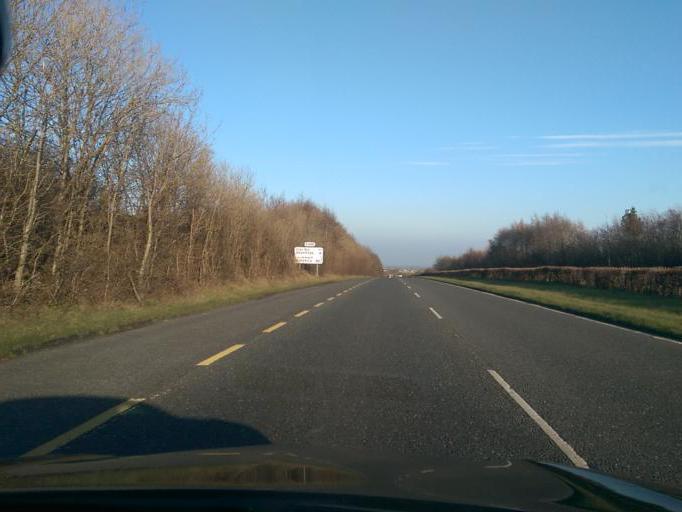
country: IE
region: Connaught
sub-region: County Galway
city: Oranmore
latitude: 53.2791
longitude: -8.9659
